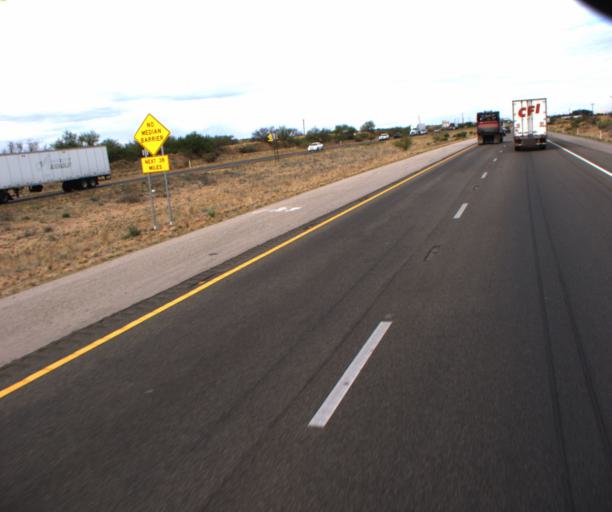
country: US
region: Arizona
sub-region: Cochise County
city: Whetstone
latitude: 31.9635
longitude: -110.3670
